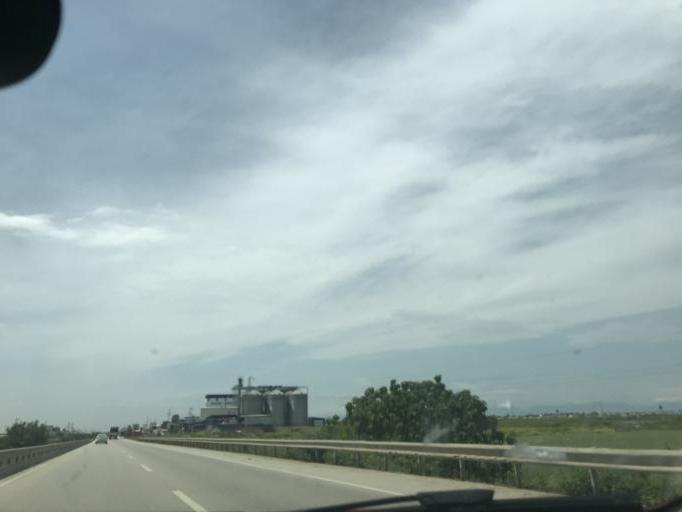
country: TR
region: Adana
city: Yuregir
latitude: 36.9776
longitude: 35.4714
